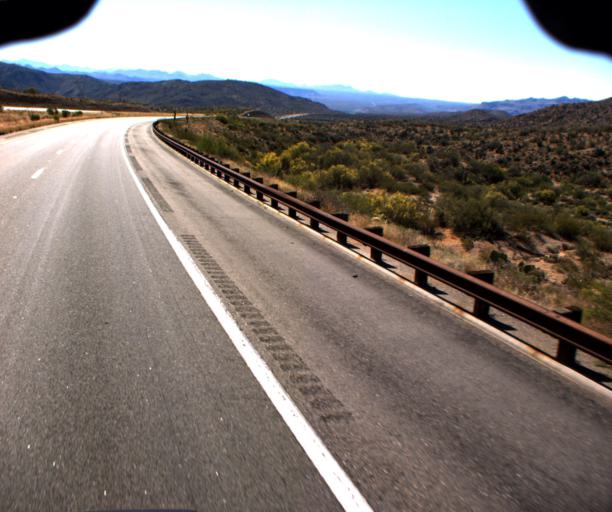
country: US
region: Arizona
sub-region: Yavapai County
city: Bagdad
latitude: 34.4392
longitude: -113.2634
